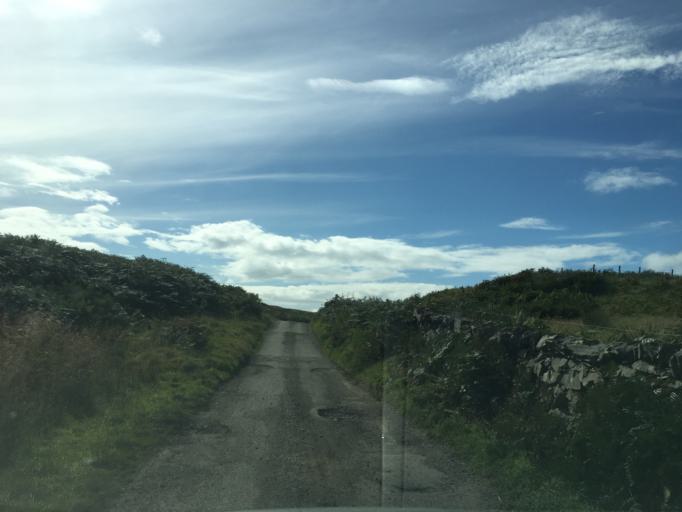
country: GB
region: Scotland
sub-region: Argyll and Bute
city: Oban
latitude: 56.2465
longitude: -5.6319
